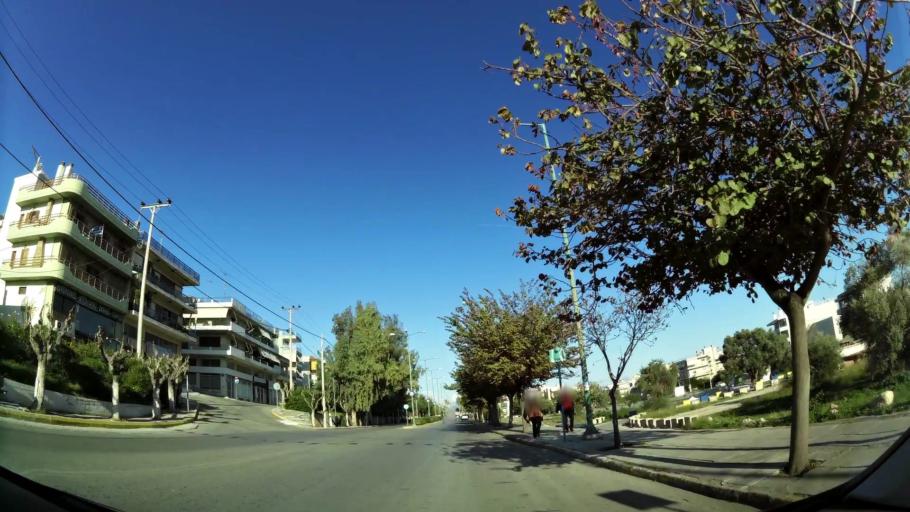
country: GR
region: Attica
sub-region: Nomarchia Anatolikis Attikis
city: Rafina
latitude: 38.0190
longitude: 24.0039
